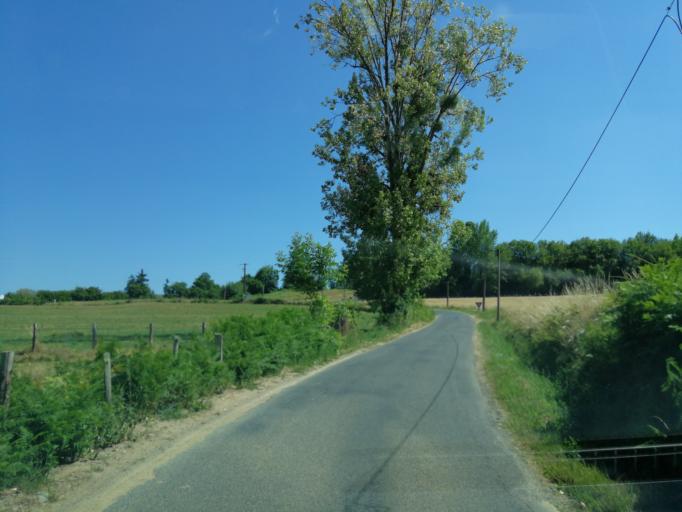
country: FR
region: Limousin
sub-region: Departement de la Correze
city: Sainte-Fereole
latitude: 45.2331
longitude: 1.5951
